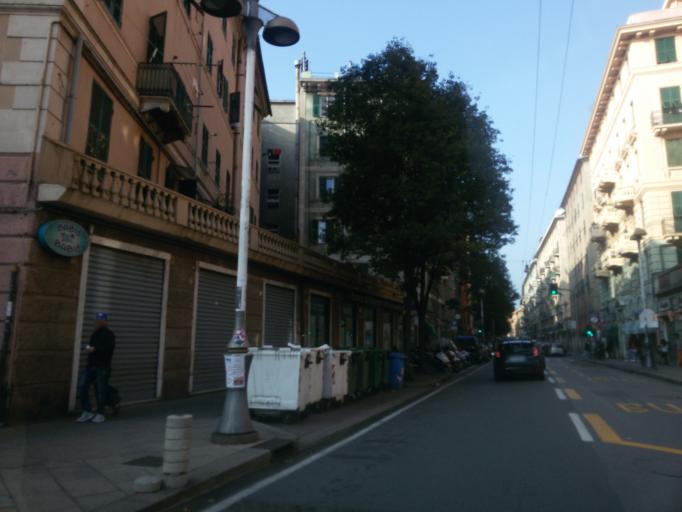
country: IT
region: Liguria
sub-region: Provincia di Genova
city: Genoa
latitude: 44.4289
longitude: 8.8934
